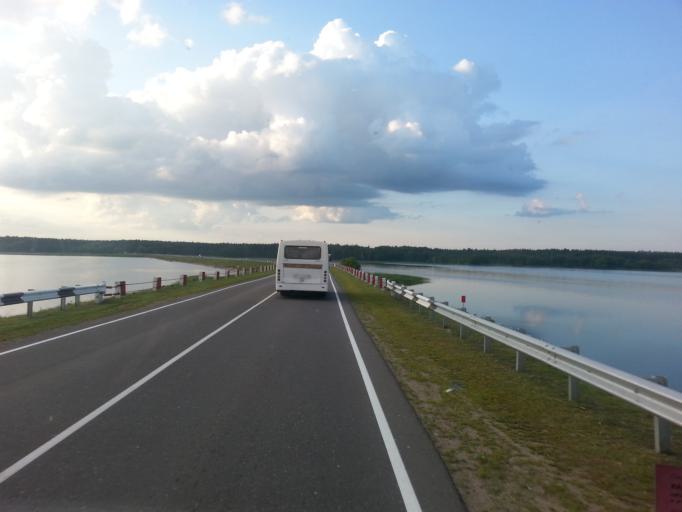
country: BY
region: Minsk
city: Il'ya
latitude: 54.5053
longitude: 27.2283
